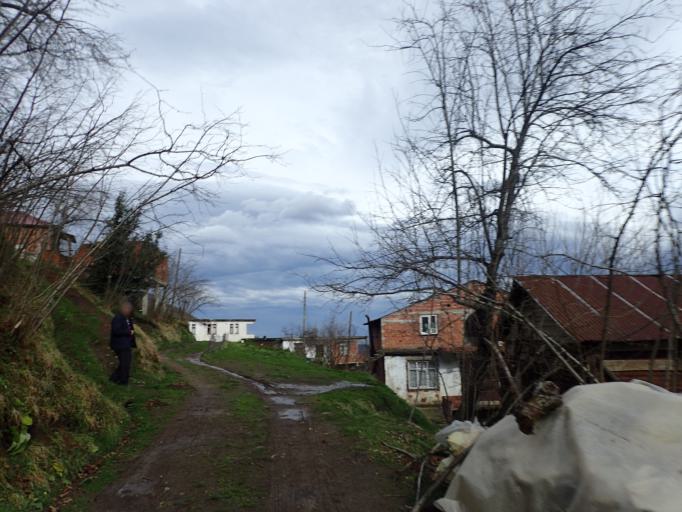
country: TR
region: Ordu
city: Camas
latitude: 40.8912
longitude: 37.5777
